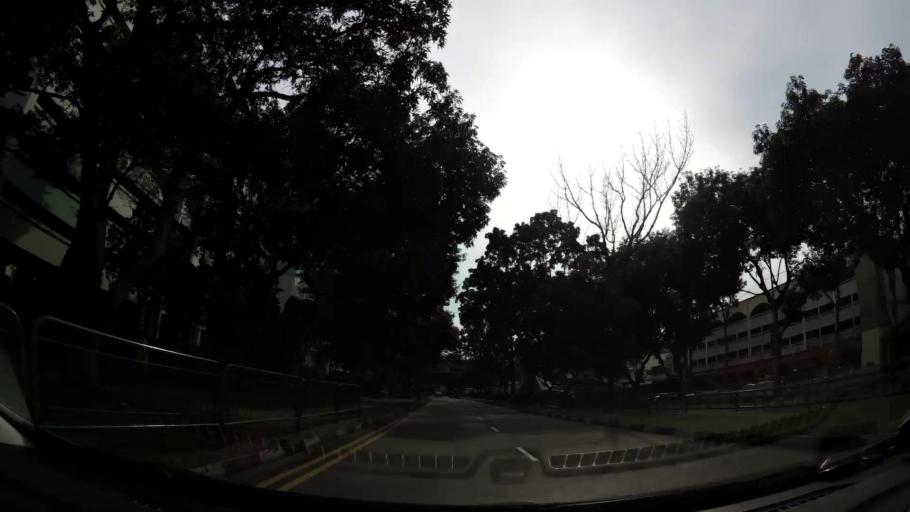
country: SG
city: Singapore
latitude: 1.3741
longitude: 103.8876
